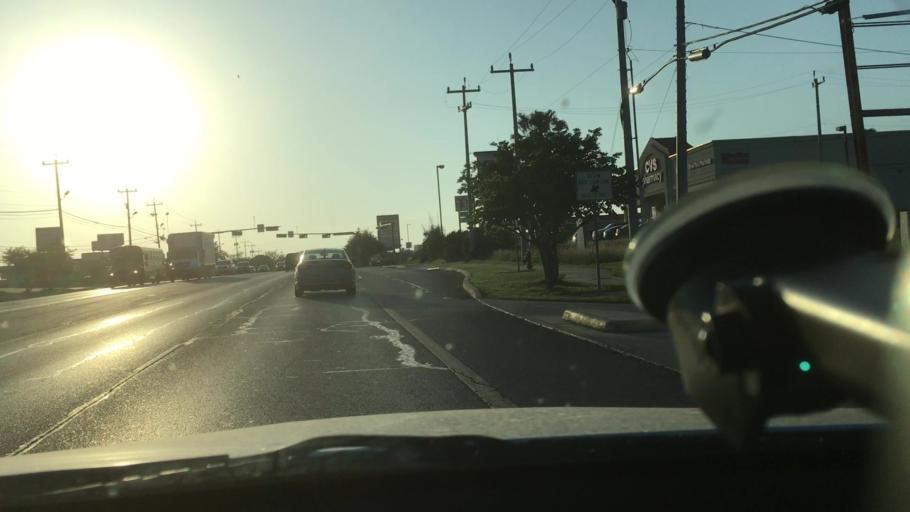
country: US
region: Texas
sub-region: Bexar County
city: Universal City
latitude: 29.5533
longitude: -98.3080
